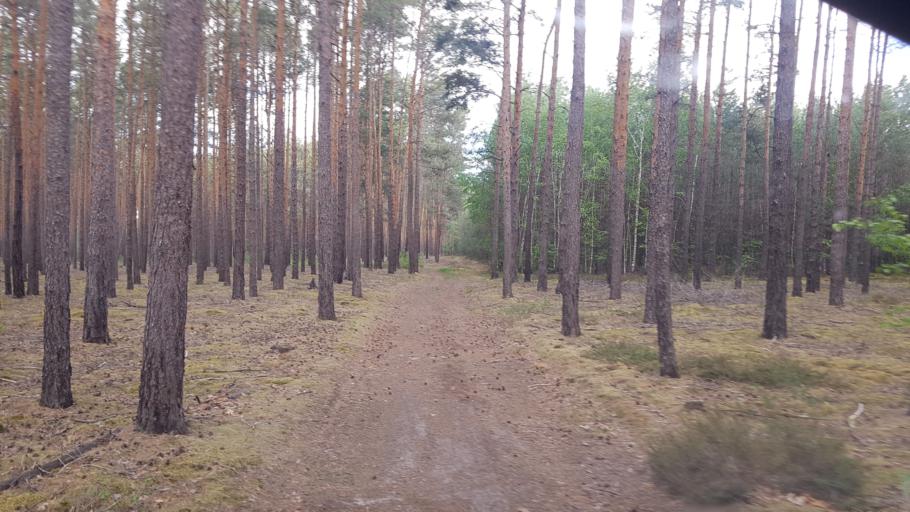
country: DE
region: Brandenburg
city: Finsterwalde
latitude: 51.6411
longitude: 13.6634
